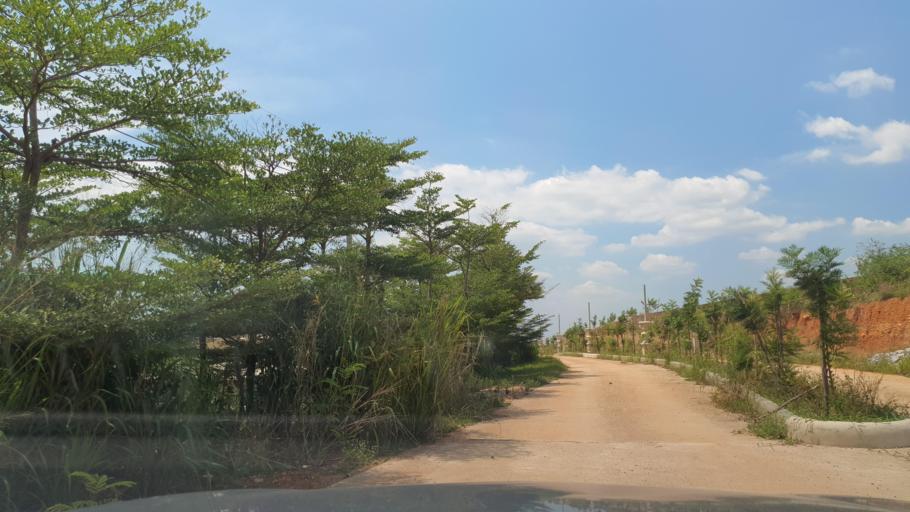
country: TH
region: Rayong
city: Ban Chang
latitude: 12.7505
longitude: 100.9642
